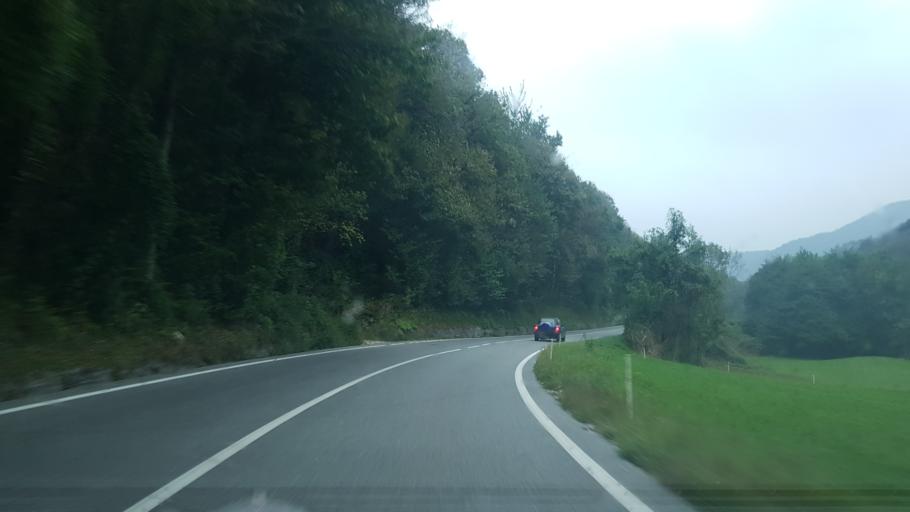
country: IT
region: Piedmont
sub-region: Provincia di Cuneo
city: Frabosa Sottana
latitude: 44.2957
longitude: 7.7884
